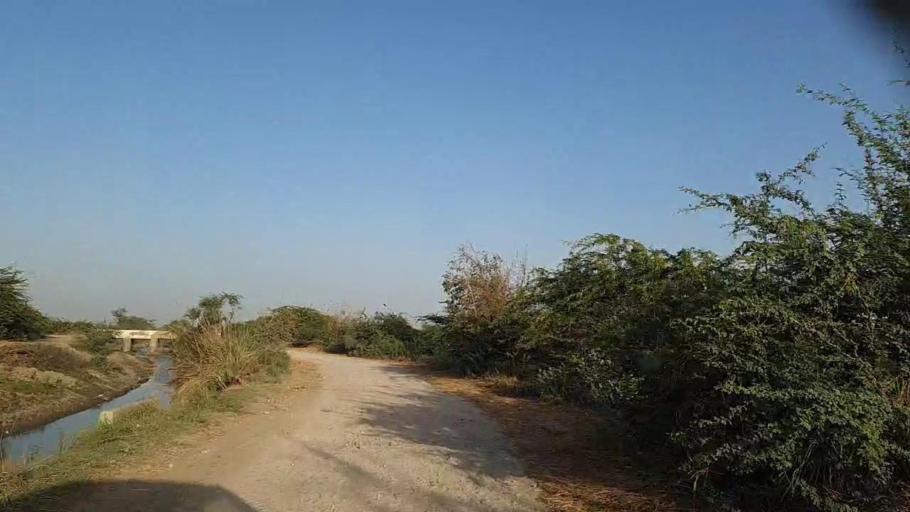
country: PK
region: Sindh
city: Jati
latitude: 24.4135
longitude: 68.3265
